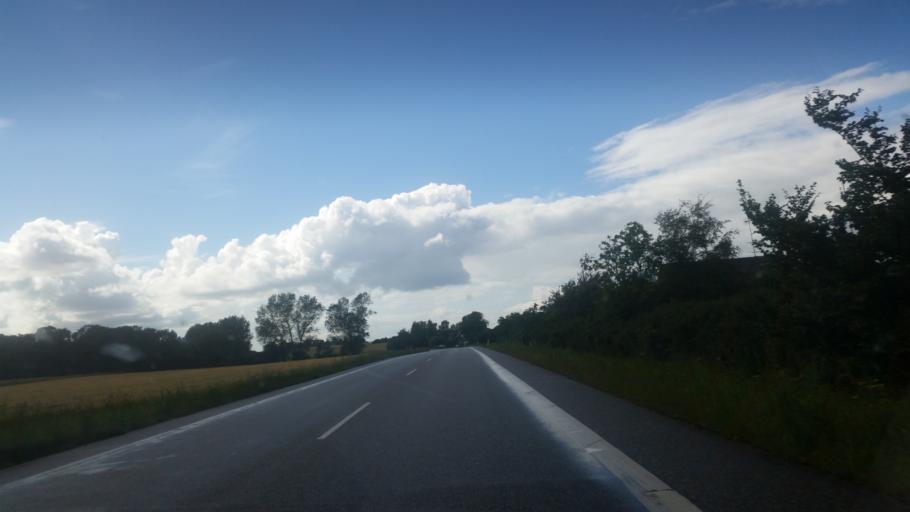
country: DK
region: Zealand
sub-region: Holbaek Kommune
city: Svinninge
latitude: 55.7266
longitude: 11.5812
